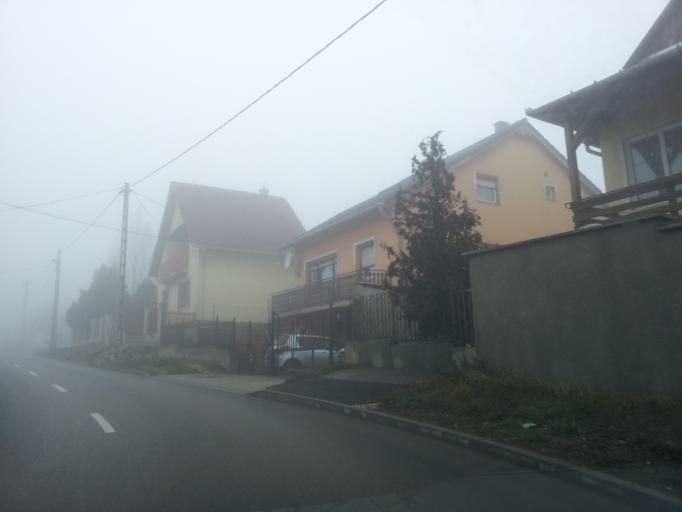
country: HU
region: Pest
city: Erd
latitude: 47.4065
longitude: 18.9092
